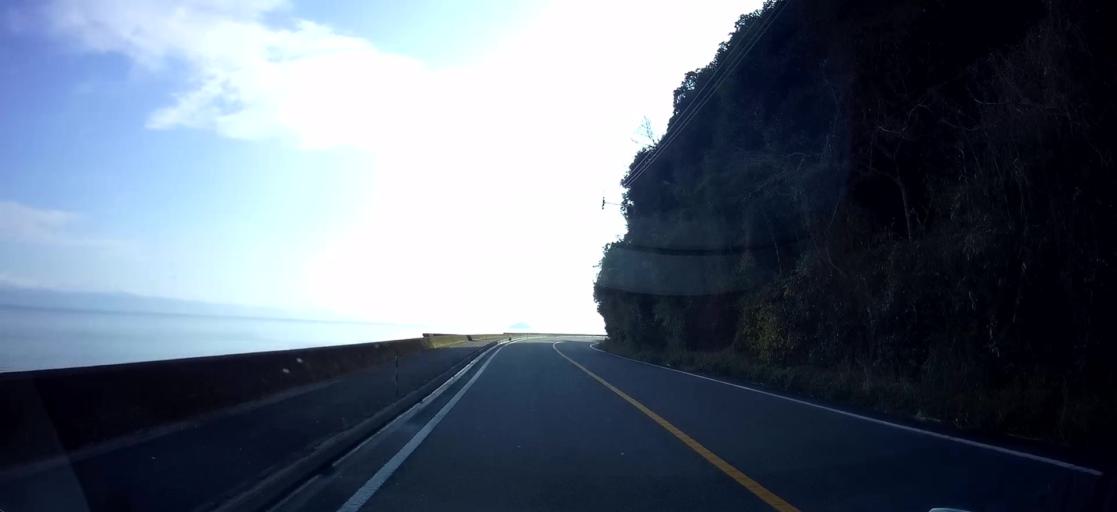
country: JP
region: Kumamoto
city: Yatsushiro
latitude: 32.5053
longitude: 130.4510
